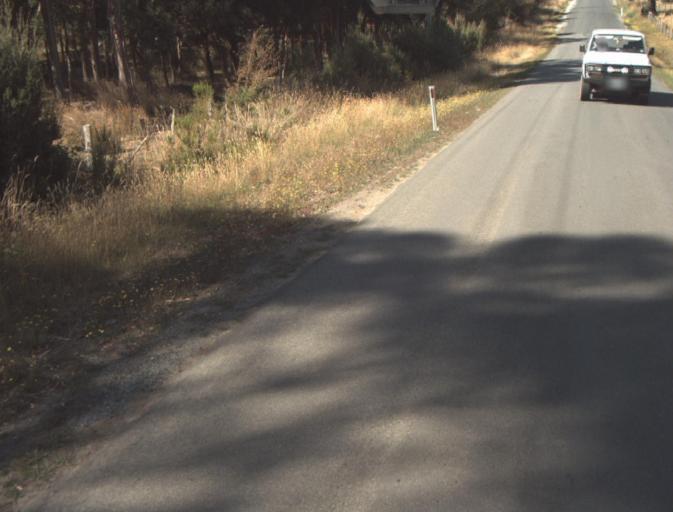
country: AU
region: Tasmania
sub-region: Launceston
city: Mayfield
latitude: -41.2363
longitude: 147.2342
